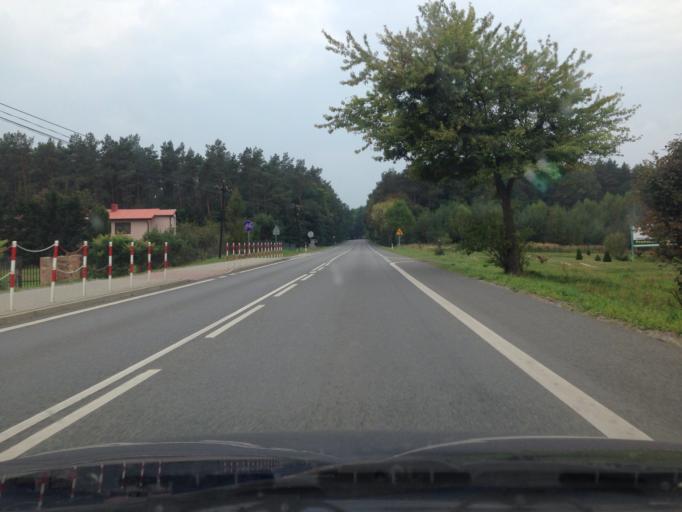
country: PL
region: Kujawsko-Pomorskie
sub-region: Powiat swiecki
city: Nowe
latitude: 53.6359
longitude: 18.6954
